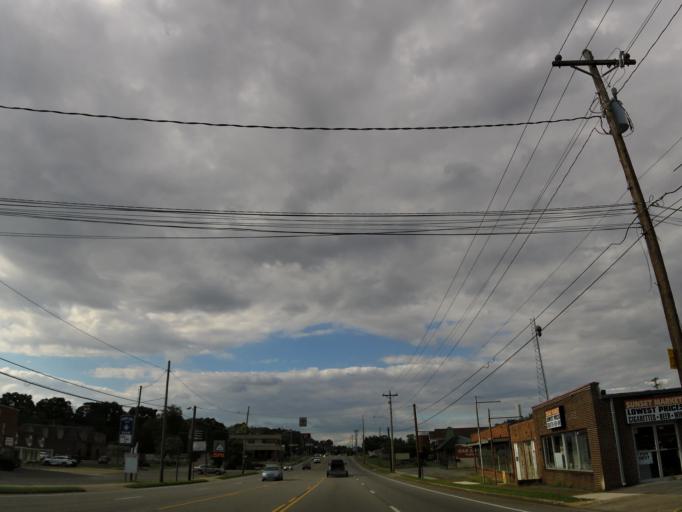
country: US
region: Georgia
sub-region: Catoosa County
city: Fort Oglethorpe
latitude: 34.9490
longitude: -85.2589
